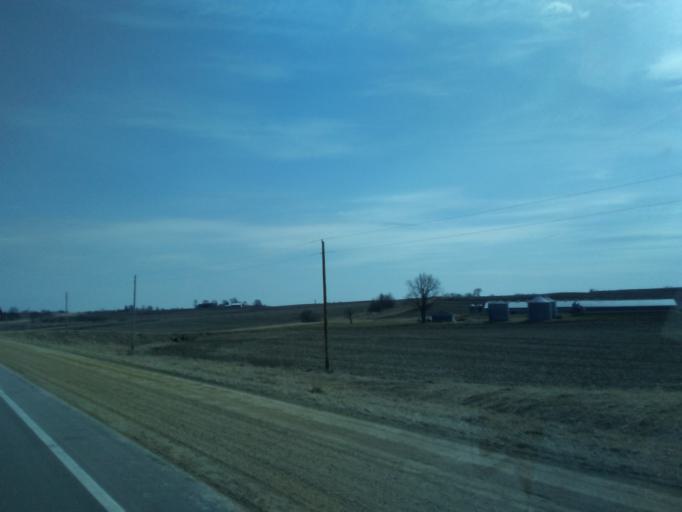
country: US
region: Iowa
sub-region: Winneshiek County
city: Decorah
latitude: 43.3979
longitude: -91.8405
